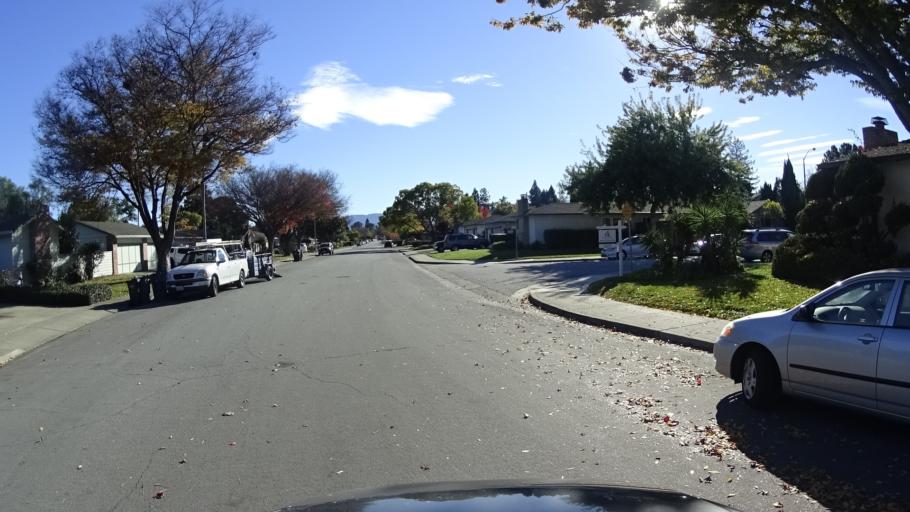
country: US
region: California
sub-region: Santa Clara County
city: Cupertino
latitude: 37.3447
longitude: -122.0313
